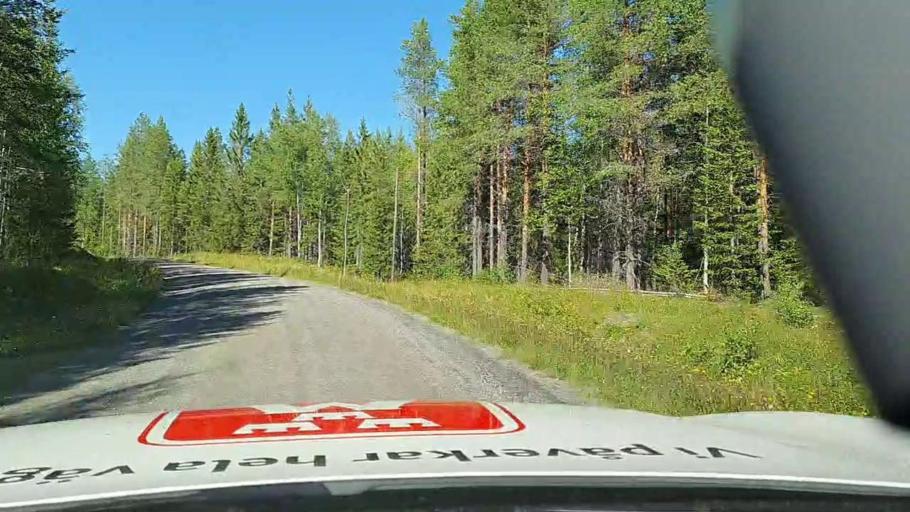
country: SE
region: Jaemtland
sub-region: OEstersunds Kommun
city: Lit
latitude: 63.7642
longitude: 14.6626
